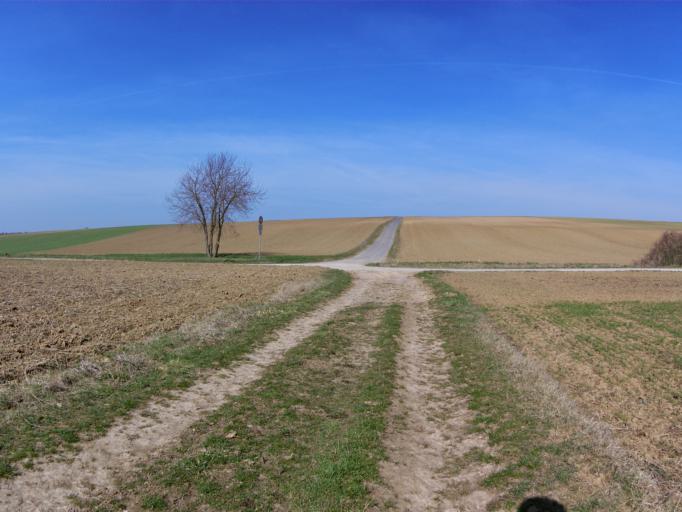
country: DE
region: Bavaria
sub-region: Regierungsbezirk Unterfranken
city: Estenfeld
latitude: 49.8112
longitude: 10.0115
